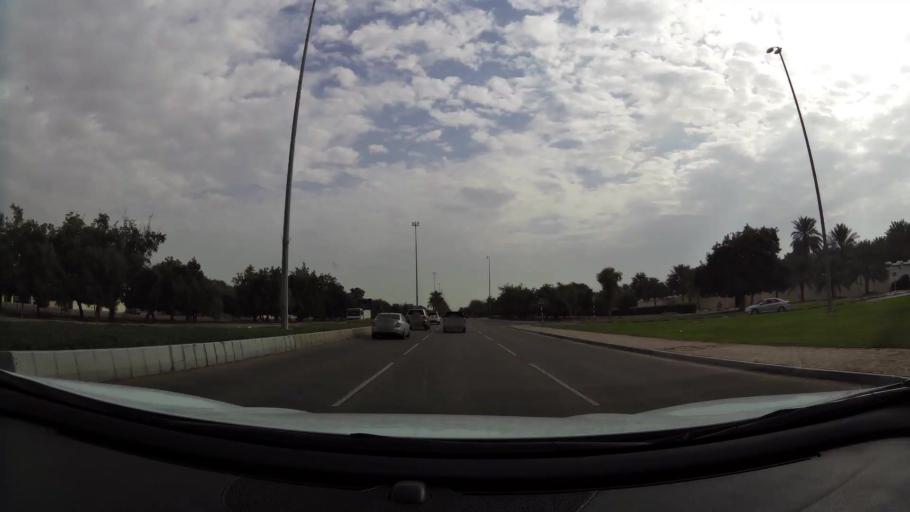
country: AE
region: Abu Dhabi
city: Al Ain
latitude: 24.2167
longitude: 55.7074
